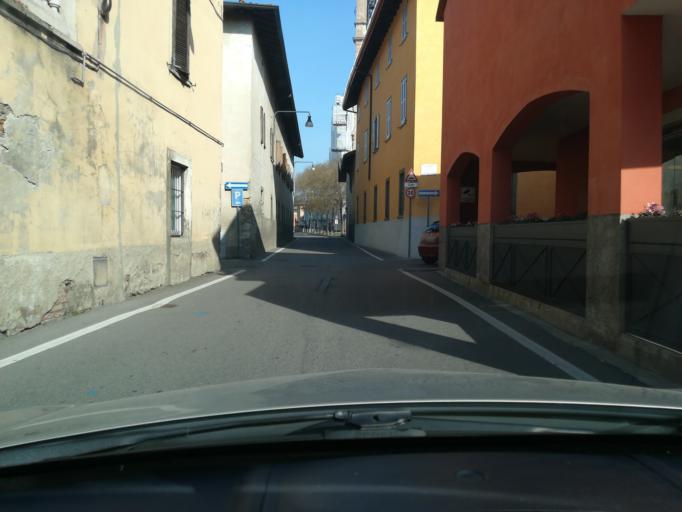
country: IT
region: Lombardy
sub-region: Provincia di Bergamo
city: Stezzano
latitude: 45.6492
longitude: 9.6523
